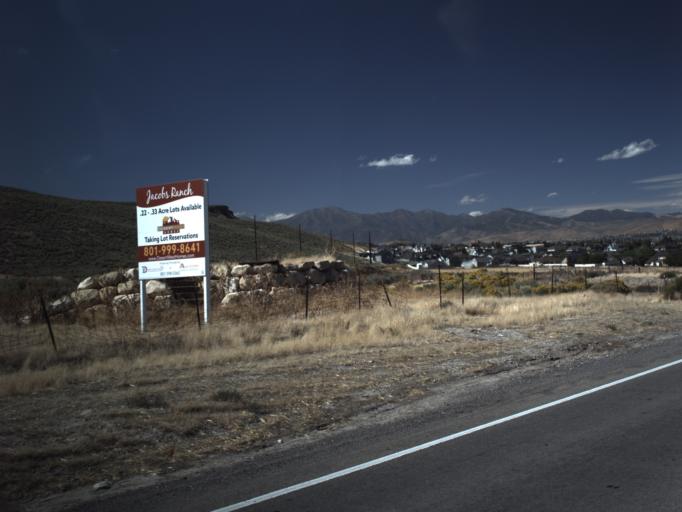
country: US
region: Utah
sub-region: Utah County
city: Saratoga Springs
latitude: 40.3290
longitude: -111.9079
